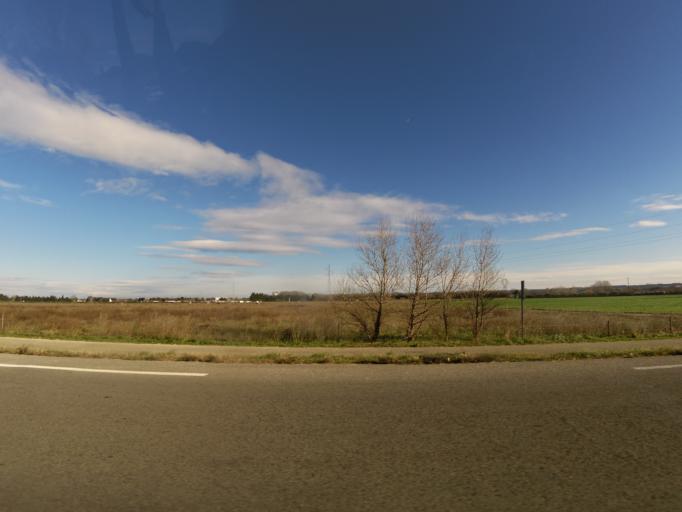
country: FR
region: Languedoc-Roussillon
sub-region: Departement du Gard
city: Milhaud
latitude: 43.7907
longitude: 4.3191
